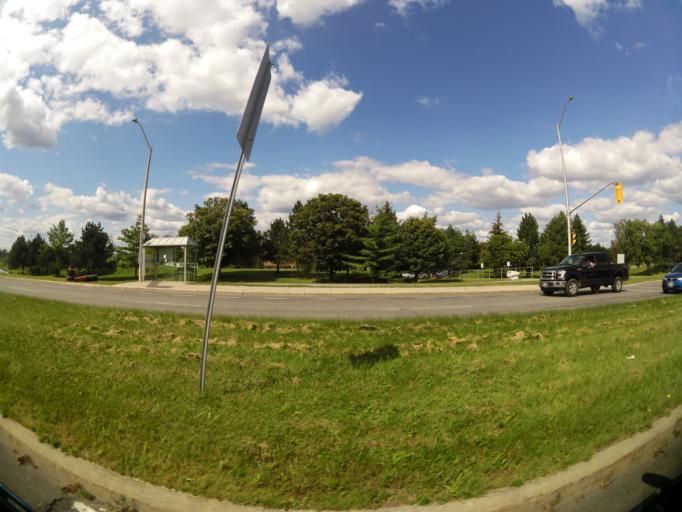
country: CA
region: Ontario
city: Bells Corners
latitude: 45.3329
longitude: -75.8068
